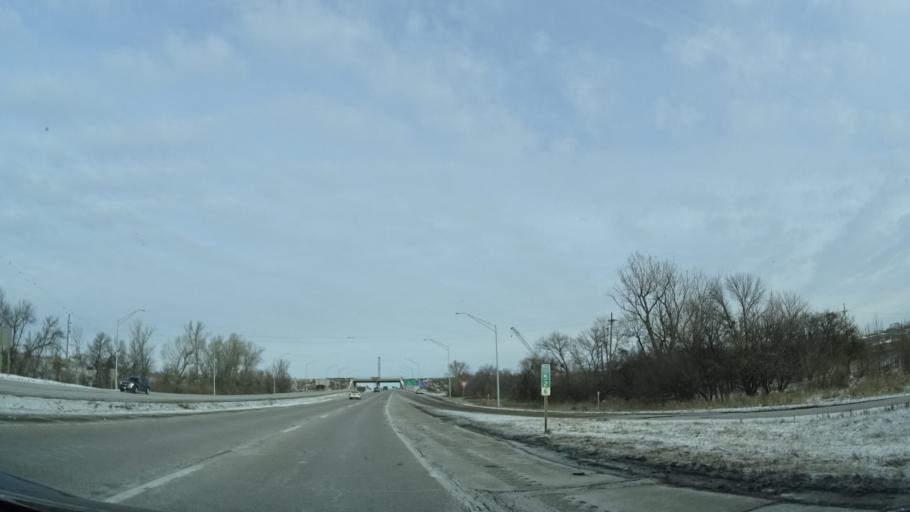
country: US
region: Nebraska
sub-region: Douglas County
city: Omaha
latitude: 41.2459
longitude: -95.9066
